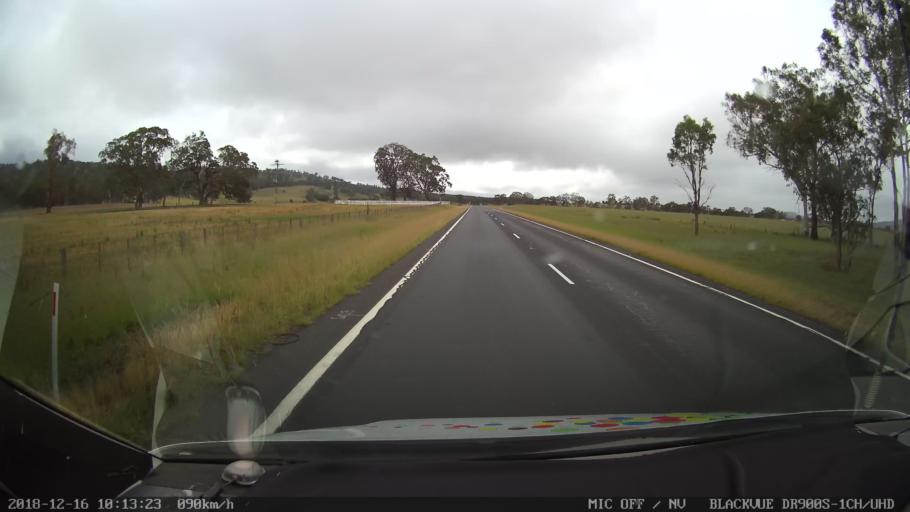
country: AU
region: New South Wales
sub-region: Glen Innes Severn
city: Glen Innes
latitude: -29.2978
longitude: 151.9519
